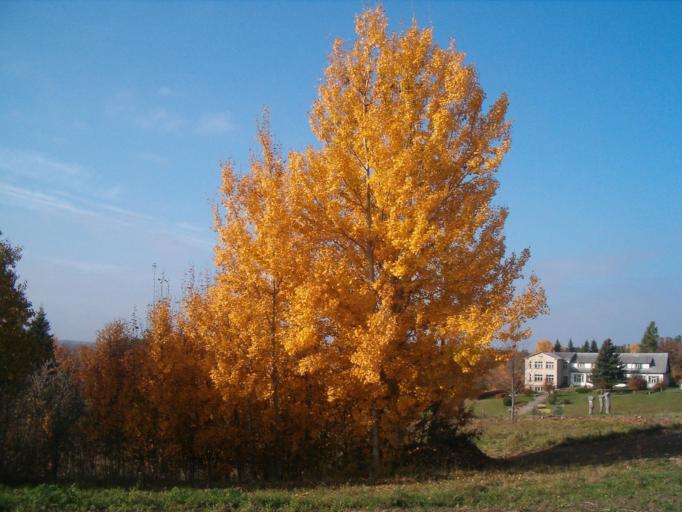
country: LT
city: Zarasai
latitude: 55.6601
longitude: 26.0608
